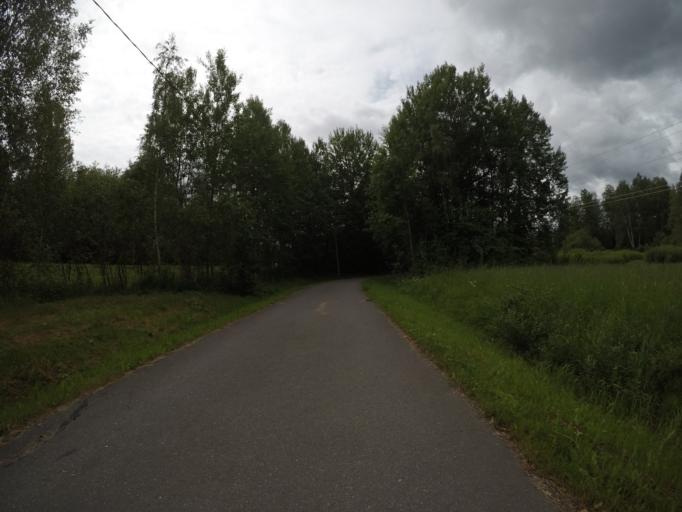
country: FI
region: Haeme
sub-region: Haemeenlinna
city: Haemeenlinna
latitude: 60.9971
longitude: 24.4954
